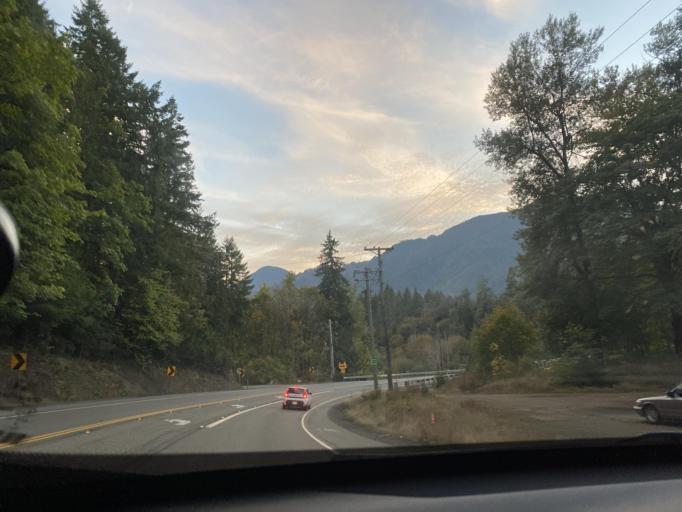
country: US
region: Washington
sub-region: Clallam County
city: Port Angeles
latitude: 48.0661
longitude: -123.5760
